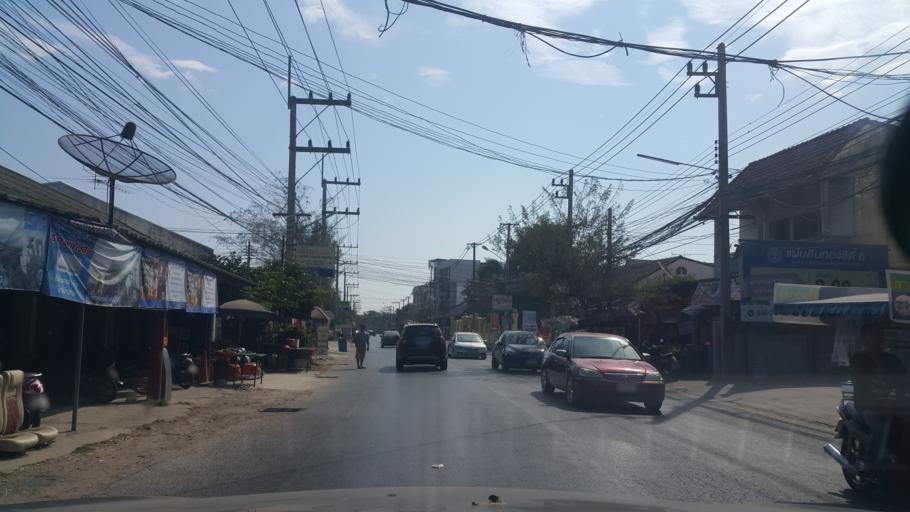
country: TH
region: Nakhon Ratchasima
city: Nakhon Ratchasima
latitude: 14.9481
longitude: 102.0499
